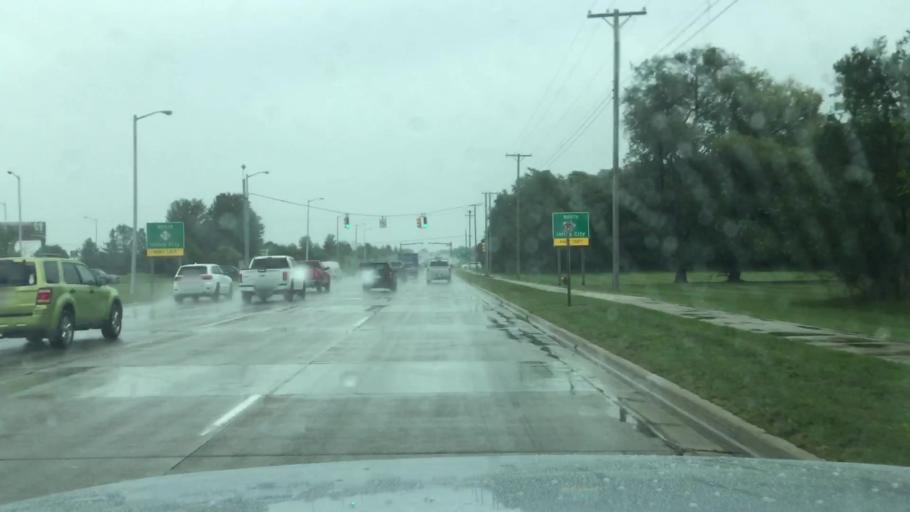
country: US
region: Michigan
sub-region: Macomb County
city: Utica
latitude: 42.6253
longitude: -83.0203
